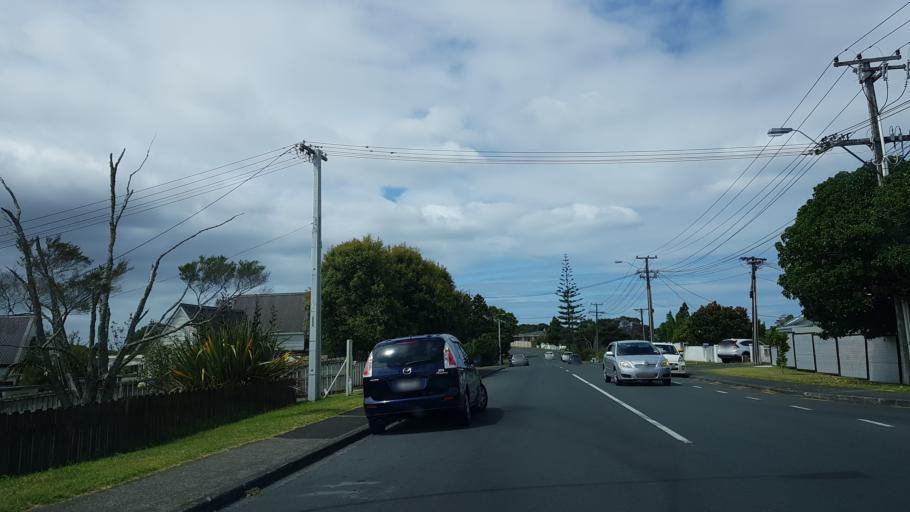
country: NZ
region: Auckland
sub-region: Auckland
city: North Shore
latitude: -36.7790
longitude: 174.7085
